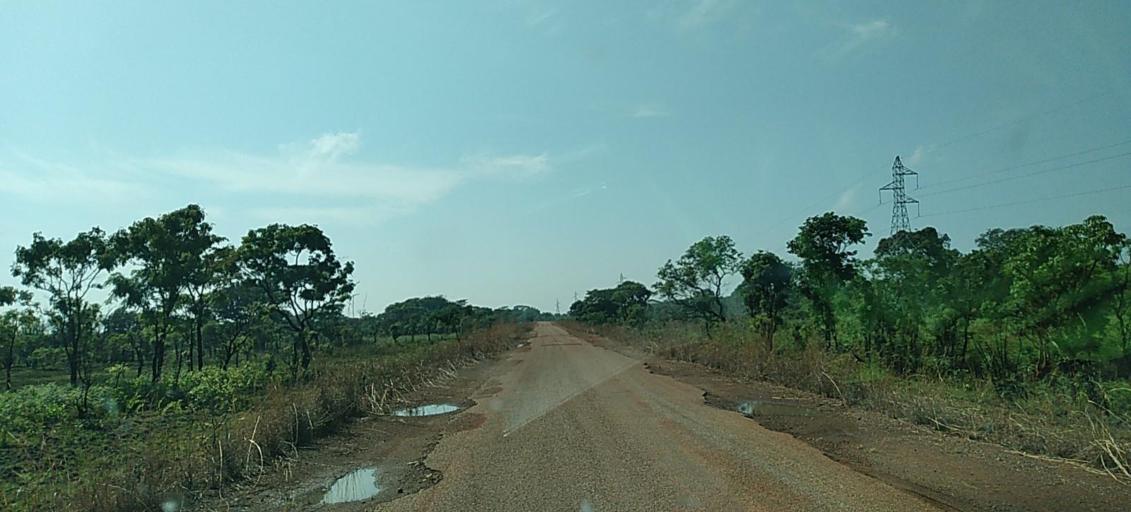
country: ZM
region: North-Western
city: Mwinilunga
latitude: -11.8167
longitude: 25.0917
